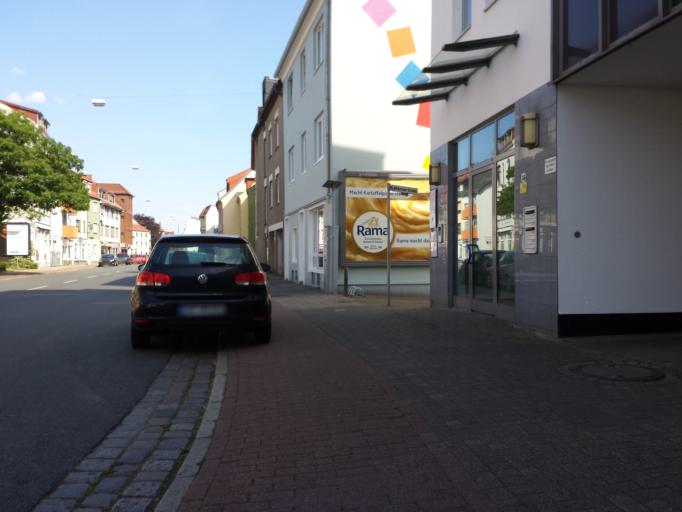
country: DE
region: Bremen
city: Bremen
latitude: 53.0826
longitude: 8.7693
